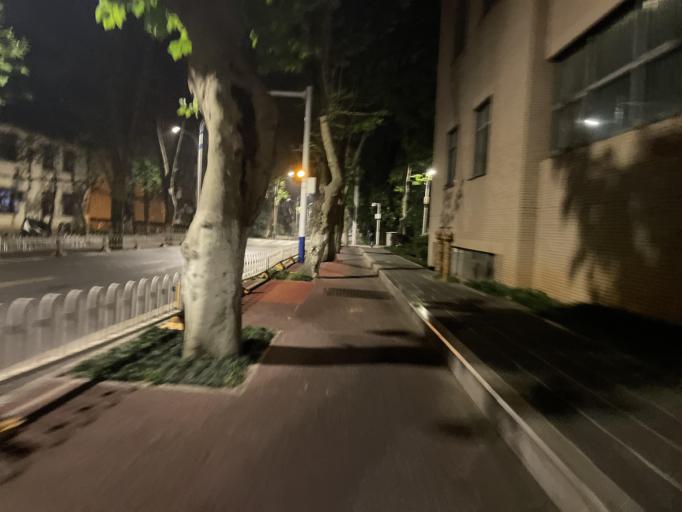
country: CN
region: Hubei
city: Guanshan
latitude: 30.5180
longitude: 114.4114
